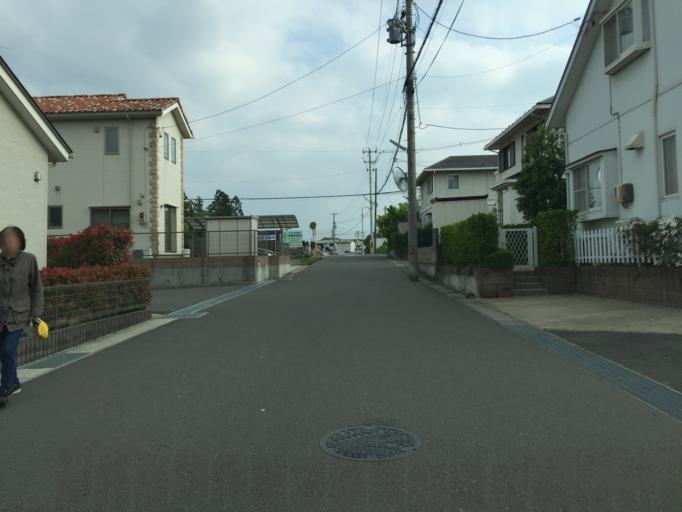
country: JP
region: Fukushima
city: Fukushima-shi
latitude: 37.7315
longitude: 140.4501
